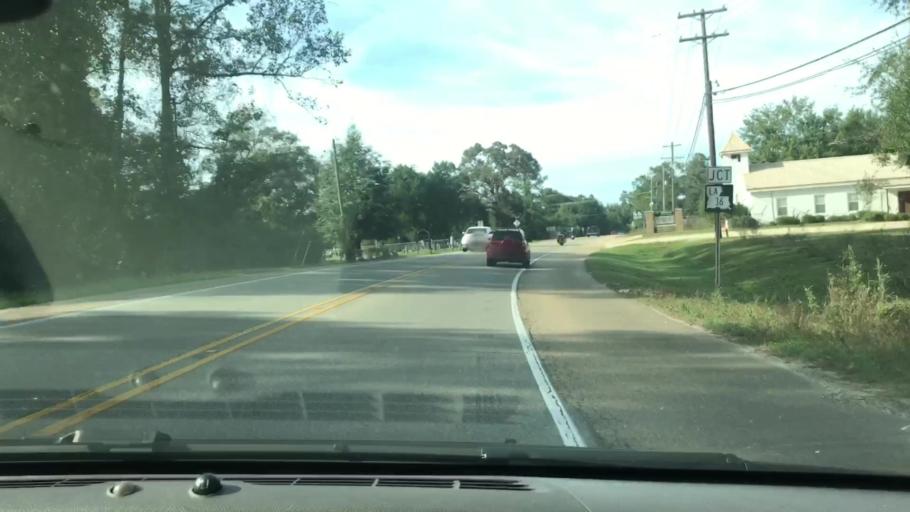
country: US
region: Louisiana
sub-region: Saint Tammany Parish
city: Pearl River
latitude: 30.4155
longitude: -89.7842
